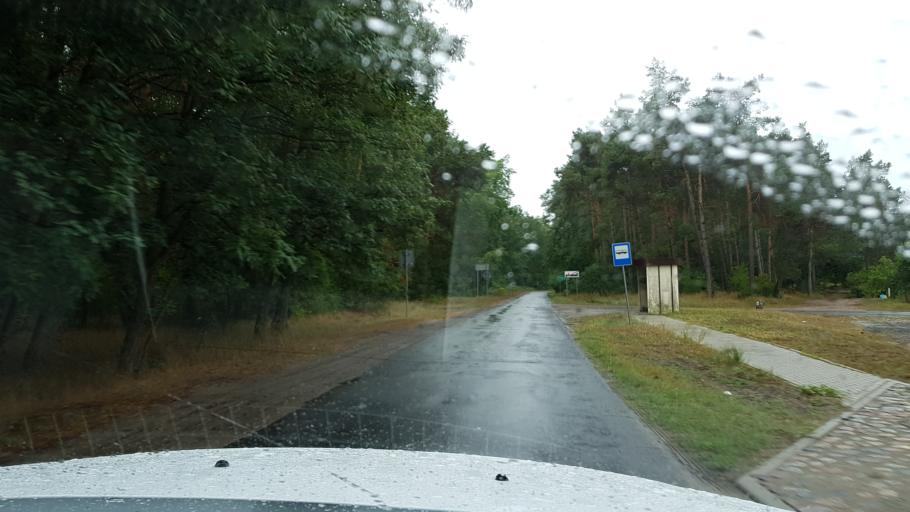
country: DE
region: Brandenburg
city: Schoneberg
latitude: 52.9714
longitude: 14.2088
